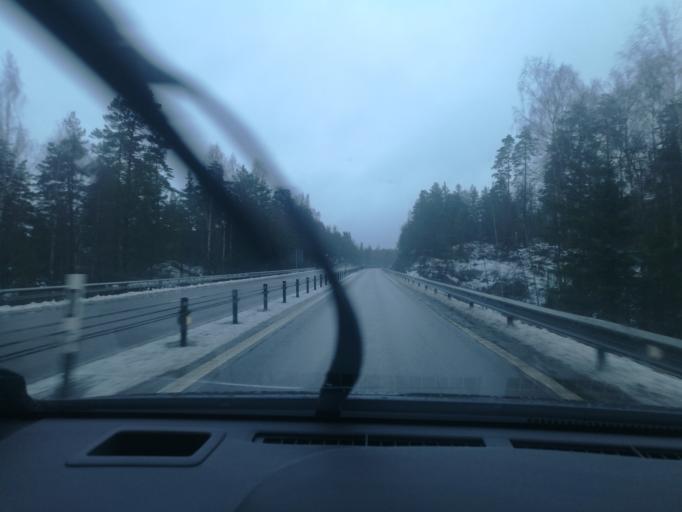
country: SE
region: OEstergoetland
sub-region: Norrkopings Kommun
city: Jursla
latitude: 58.7133
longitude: 16.1628
